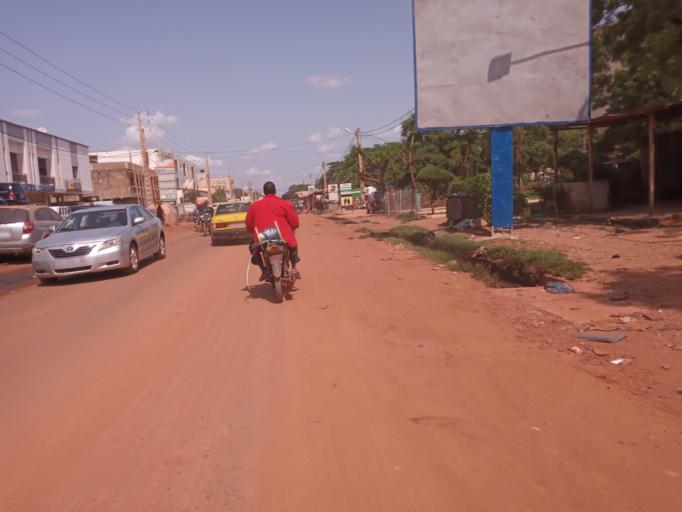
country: ML
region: Bamako
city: Bamako
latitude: 12.5972
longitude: -8.0232
